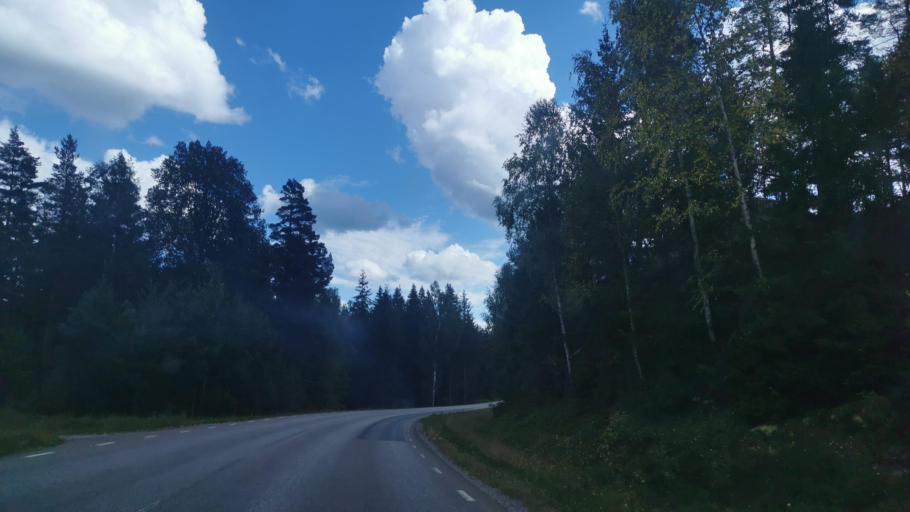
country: SE
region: OEstergoetland
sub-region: Finspangs Kommun
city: Finspang
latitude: 58.7723
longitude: 15.7885
